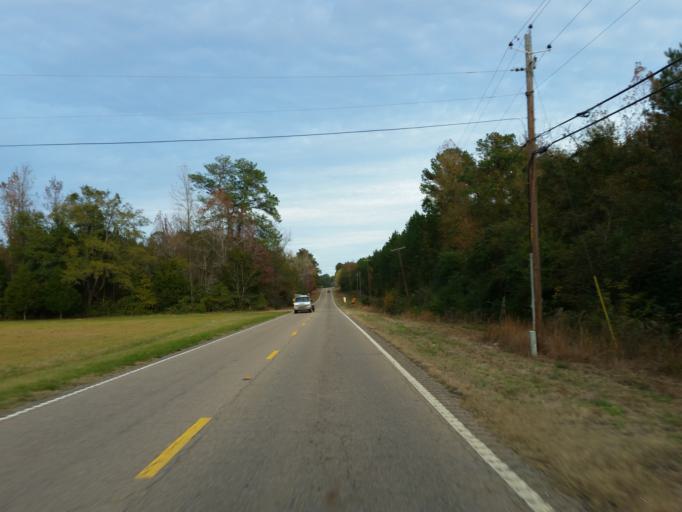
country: US
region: Mississippi
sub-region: Lauderdale County
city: Marion
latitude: 32.4068
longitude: -88.5853
